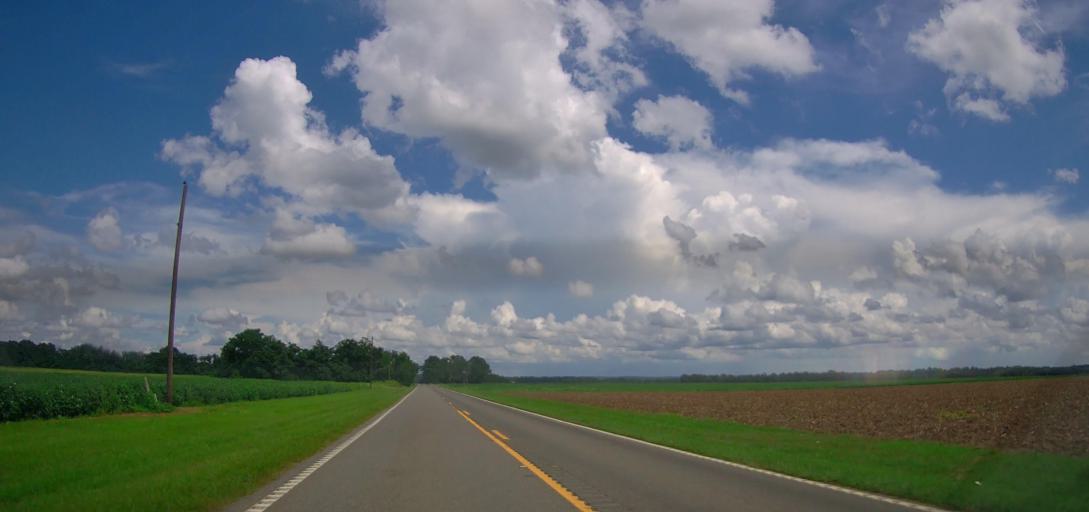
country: US
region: Georgia
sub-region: Taylor County
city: Reynolds
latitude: 32.4400
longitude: -84.0931
